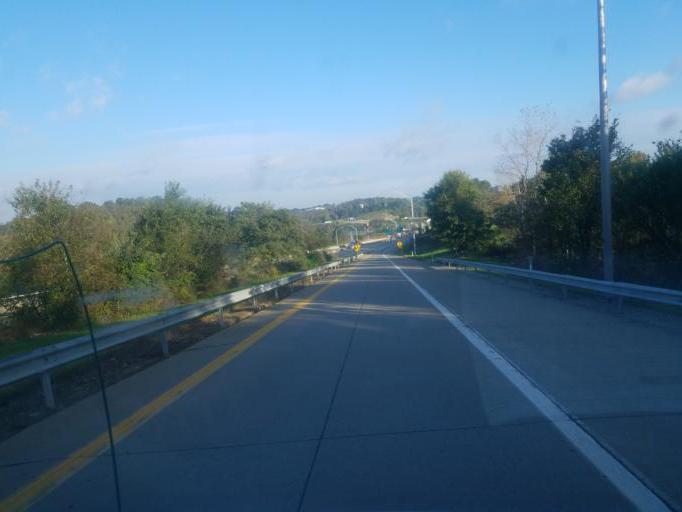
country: US
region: Pennsylvania
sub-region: Westmoreland County
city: Delmont
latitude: 40.3884
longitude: -79.5692
